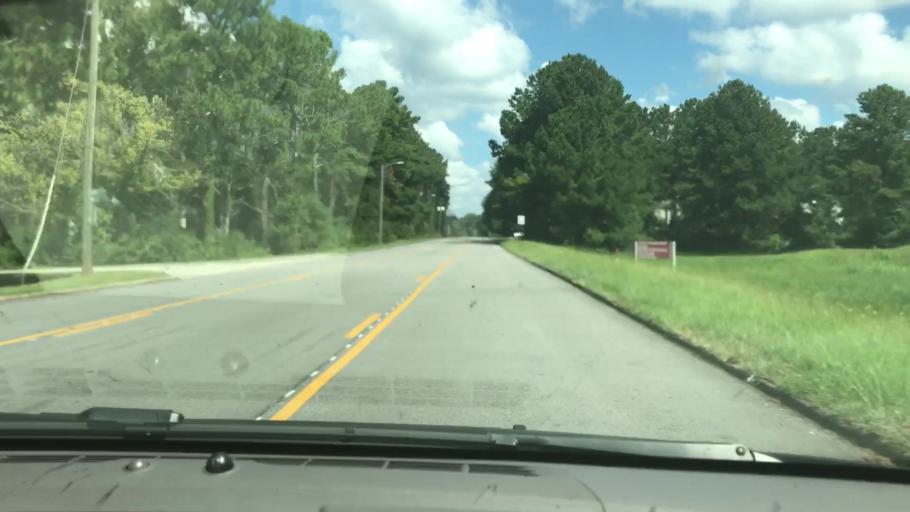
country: US
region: Georgia
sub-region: Troup County
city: La Grange
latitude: 33.0083
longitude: -85.0574
